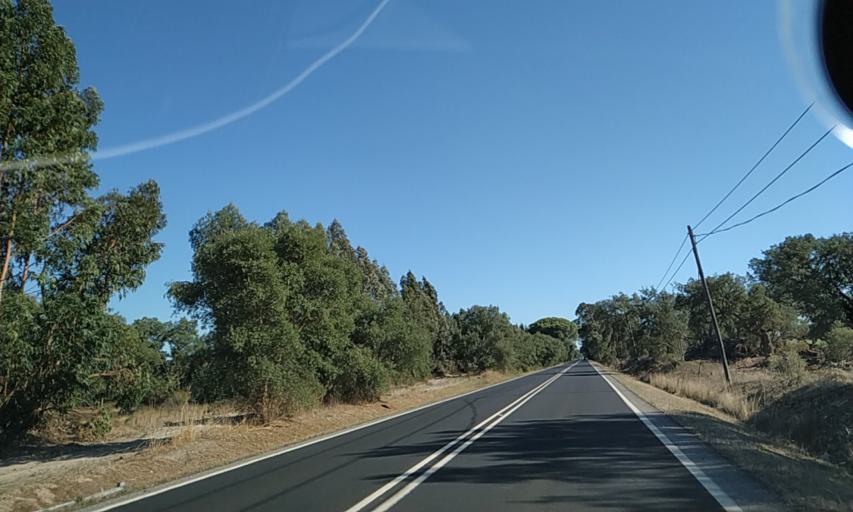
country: PT
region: Santarem
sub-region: Benavente
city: Samora Correia
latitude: 38.8566
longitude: -8.8811
